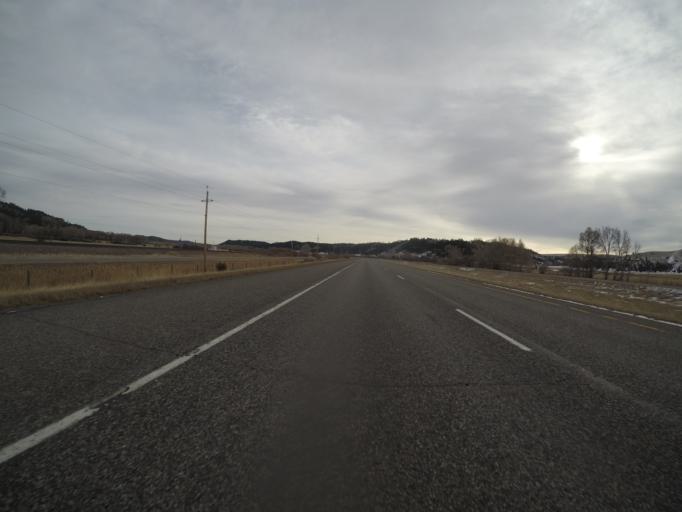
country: US
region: Montana
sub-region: Stillwater County
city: Absarokee
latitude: 45.7140
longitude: -109.6327
